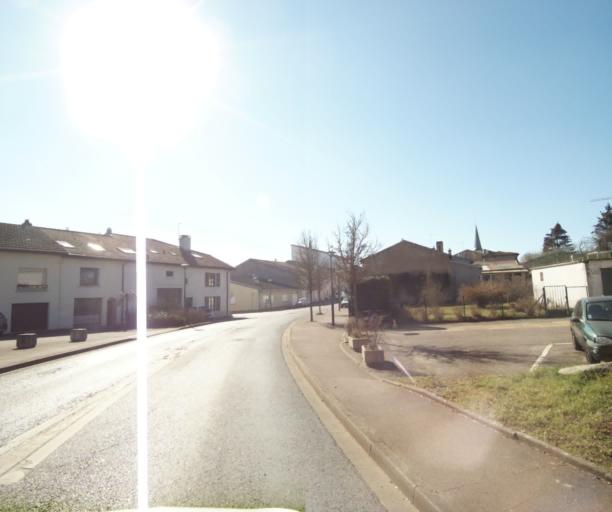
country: FR
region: Lorraine
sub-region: Departement de Meurthe-et-Moselle
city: Saulxures-les-Nancy
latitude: 48.6898
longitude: 6.2508
